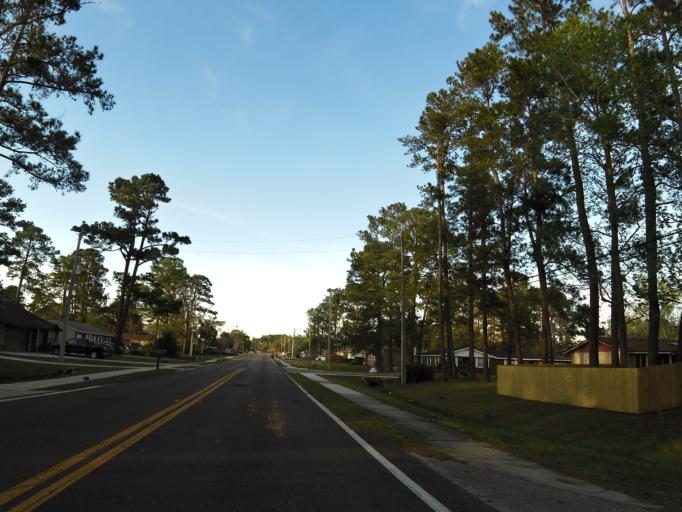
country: US
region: Florida
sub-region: Duval County
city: Jacksonville
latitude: 30.4472
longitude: -81.6708
